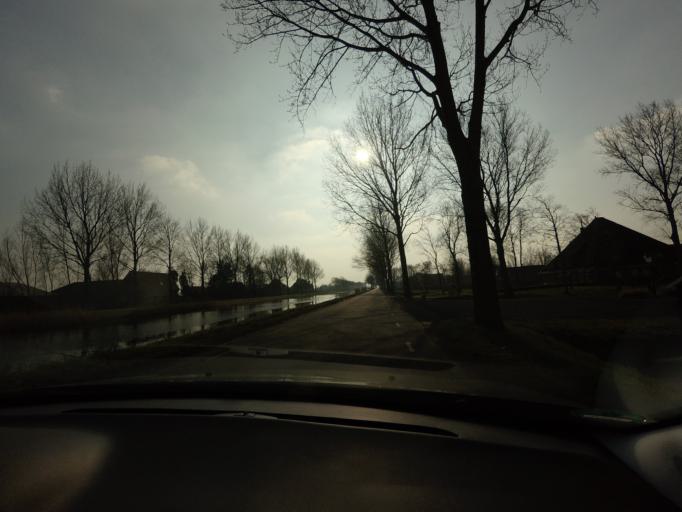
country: NL
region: North Holland
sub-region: Gemeente Alkmaar
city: Alkmaar
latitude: 52.5897
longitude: 4.7820
